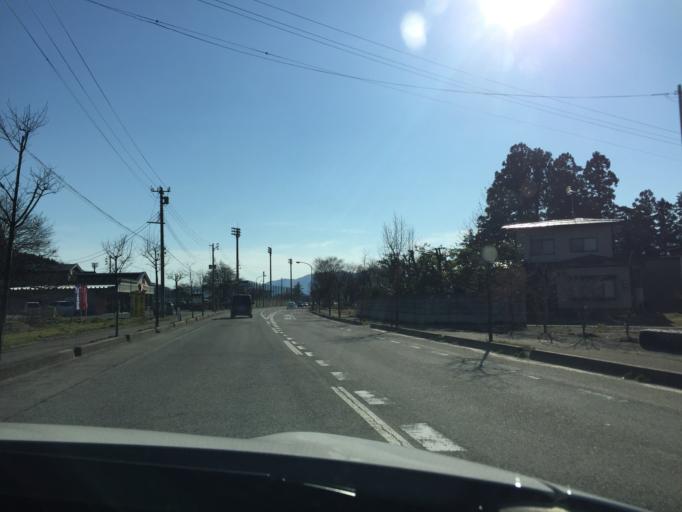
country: JP
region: Yamagata
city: Nagai
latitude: 38.1630
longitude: 140.0813
